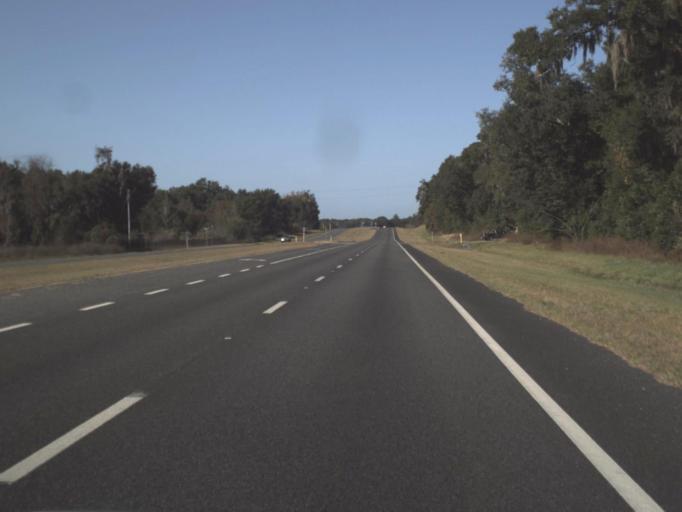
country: US
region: Florida
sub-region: Marion County
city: Belleview
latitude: 29.0294
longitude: -82.0520
